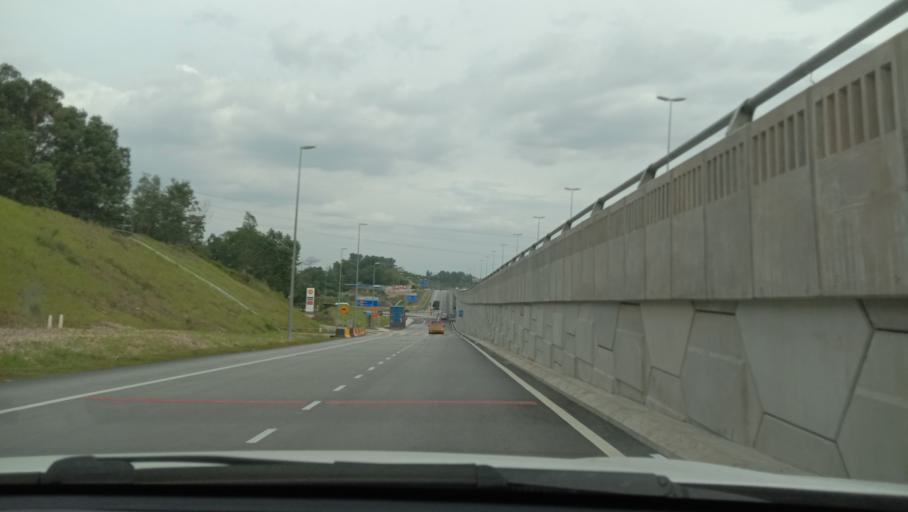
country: MY
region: Selangor
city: Kampung Baru Subang
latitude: 3.1267
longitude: 101.5178
